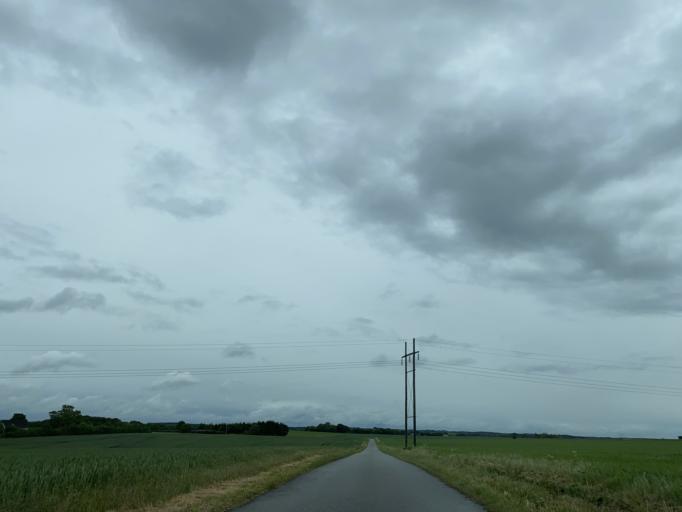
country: DK
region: Central Jutland
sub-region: Favrskov Kommune
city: Hammel
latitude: 56.2319
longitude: 9.7753
